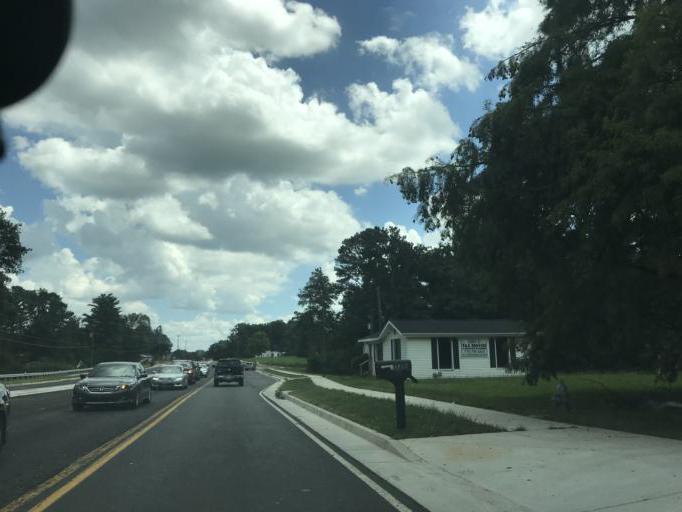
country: US
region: Georgia
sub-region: Forsyth County
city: Cumming
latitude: 34.2365
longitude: -84.1947
